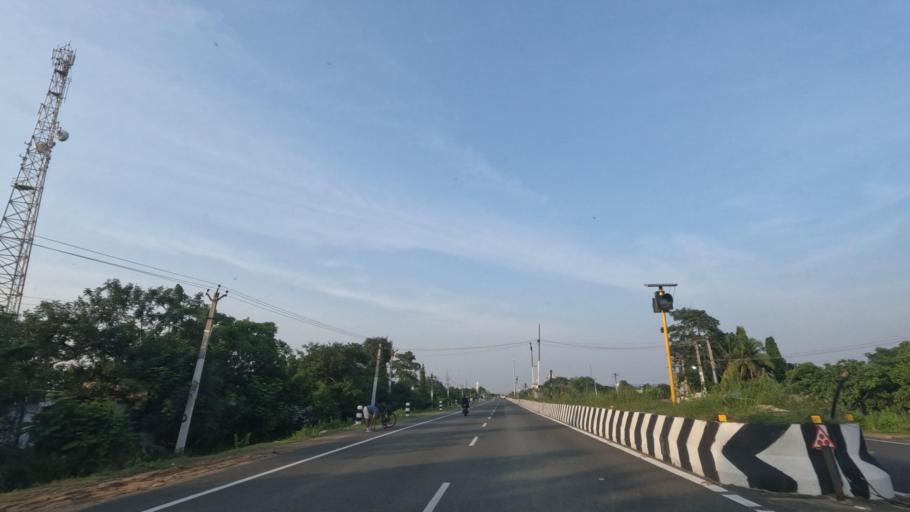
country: IN
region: Tamil Nadu
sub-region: Kancheepuram
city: Mamallapuram
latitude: 12.6957
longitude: 80.2199
